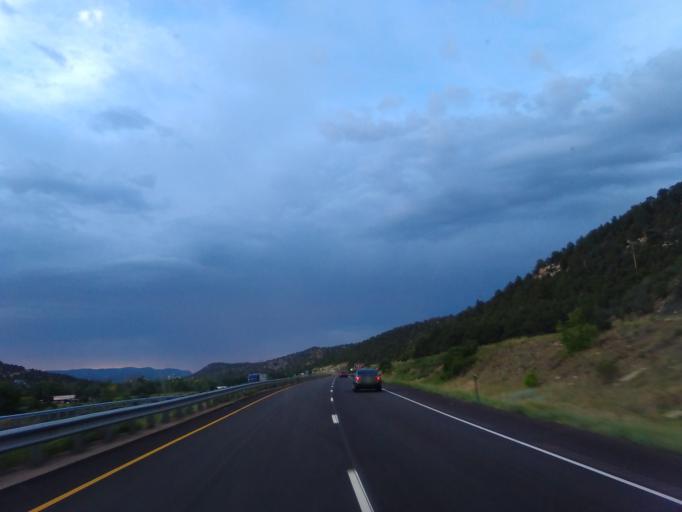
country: US
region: Colorado
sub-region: Las Animas County
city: Trinidad
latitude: 37.1065
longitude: -104.5240
